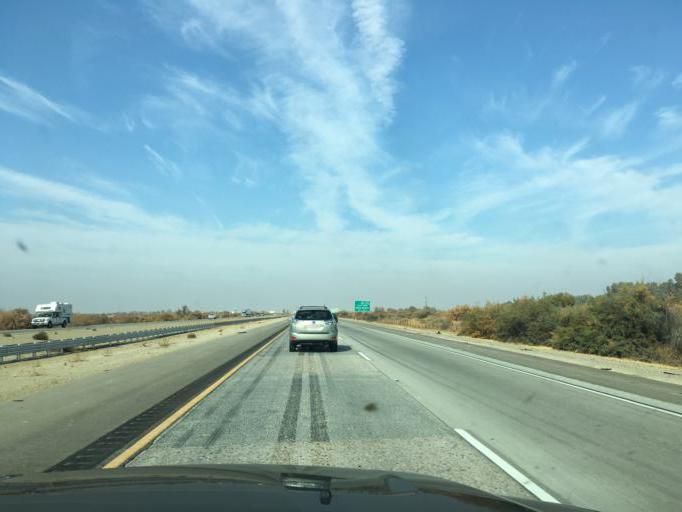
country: US
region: California
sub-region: Kern County
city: Lost Hills
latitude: 35.6016
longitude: -119.6412
